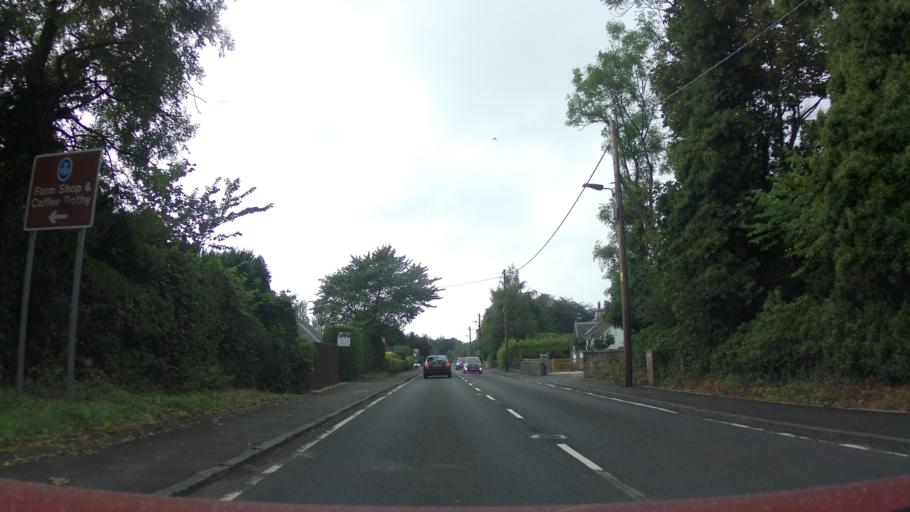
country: GB
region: Scotland
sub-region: Clackmannanshire
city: Menstrie
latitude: 56.1492
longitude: -3.8853
